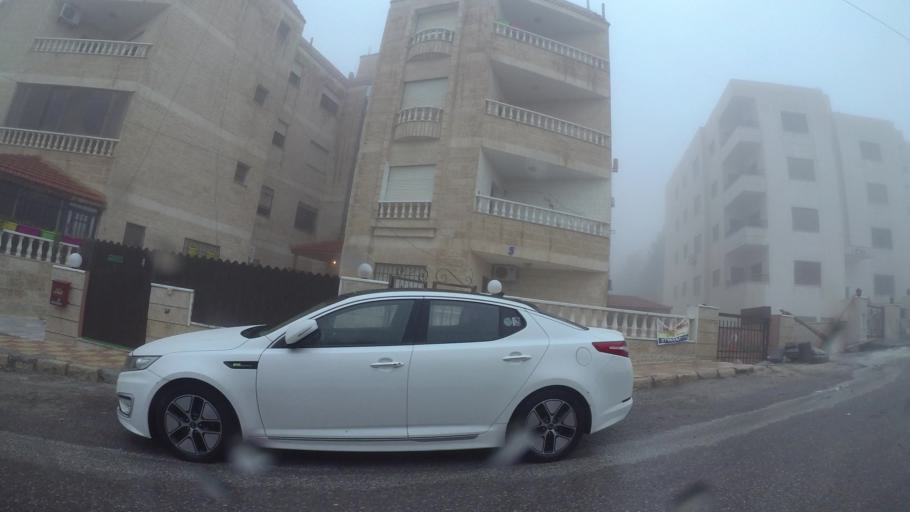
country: JO
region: Amman
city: Al Jubayhah
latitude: 32.0050
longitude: 35.8913
